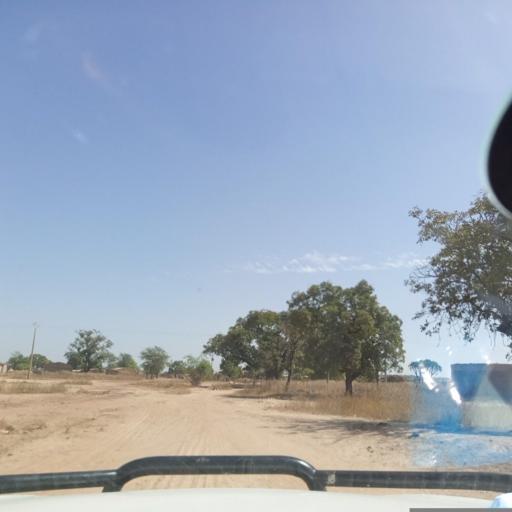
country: ML
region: Koulikoro
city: Dioila
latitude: 12.5217
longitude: -6.8112
